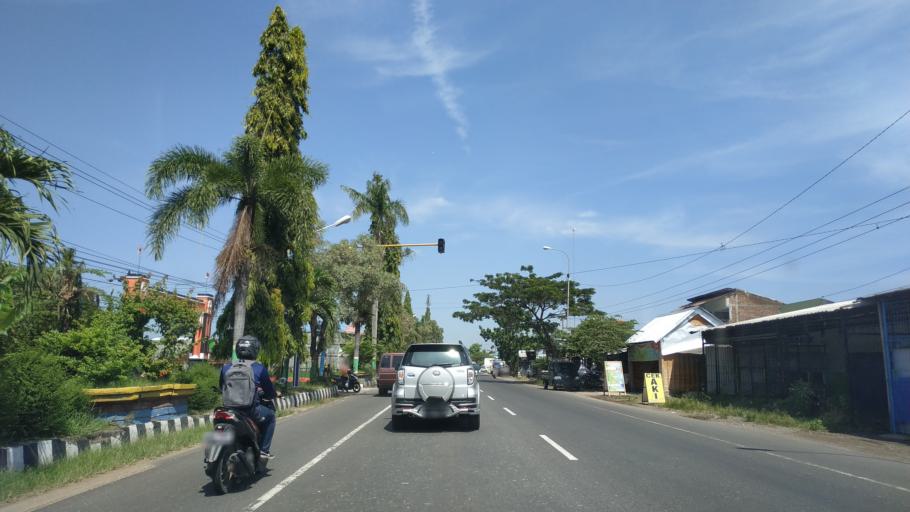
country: ID
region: Central Java
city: Geritan
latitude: -6.7494
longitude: 111.0589
